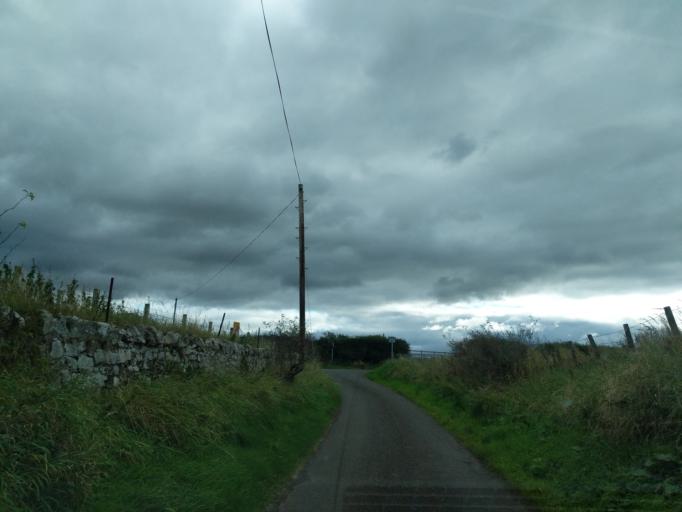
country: GB
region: Scotland
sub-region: East Lothian
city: East Linton
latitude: 55.9404
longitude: -2.7103
